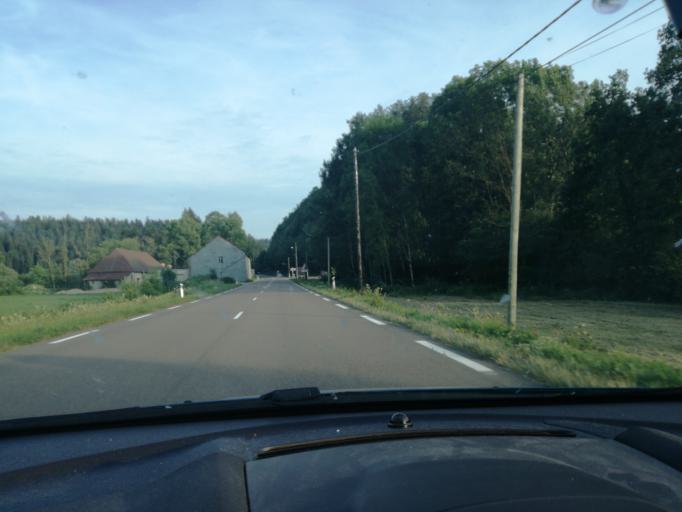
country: FR
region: Franche-Comte
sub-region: Departement du Jura
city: Champagnole
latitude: 46.6395
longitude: 5.9418
